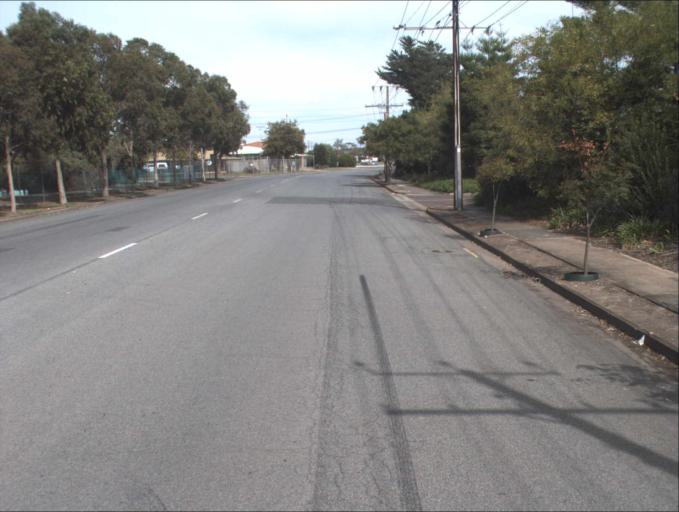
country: AU
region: South Australia
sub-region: Port Adelaide Enfield
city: Birkenhead
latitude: -34.8175
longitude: 138.5037
